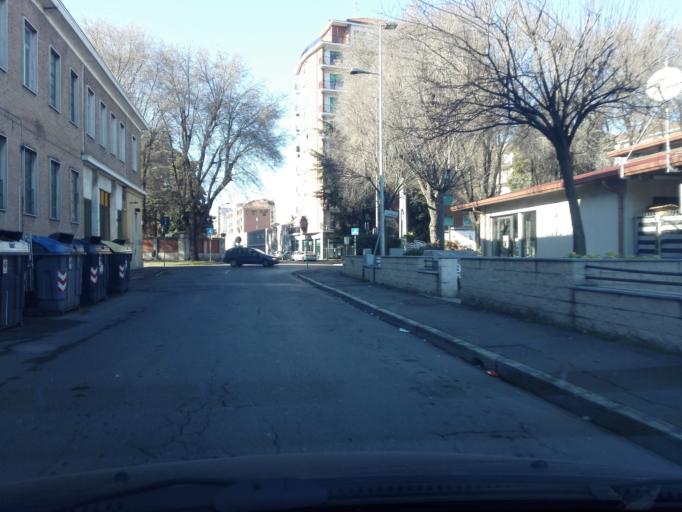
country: IT
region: Piedmont
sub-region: Provincia di Alessandria
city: Alessandria
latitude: 44.9088
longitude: 8.6306
